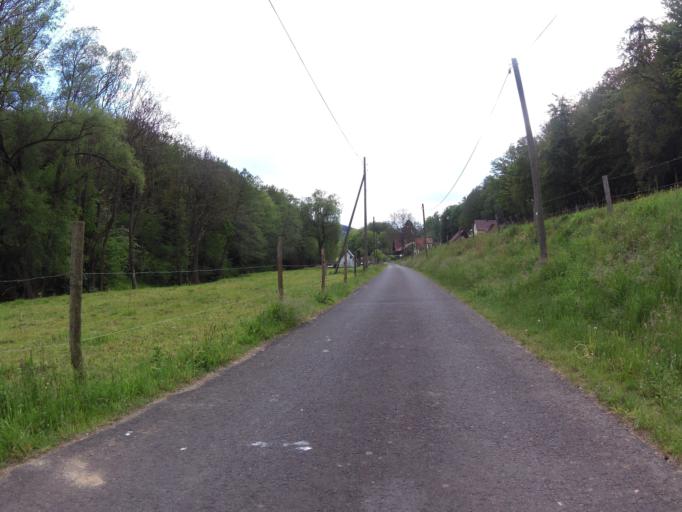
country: DE
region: Thuringia
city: Seebach
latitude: 50.9597
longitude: 10.4185
